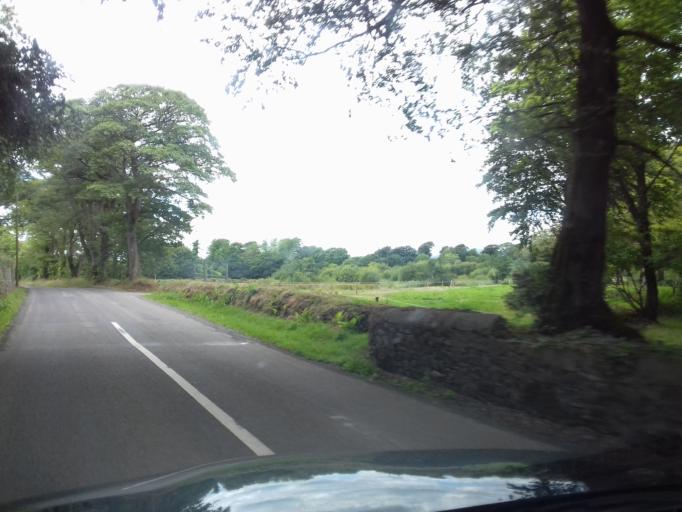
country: IE
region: Munster
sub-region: Waterford
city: Portlaw
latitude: 52.1784
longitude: -7.3421
